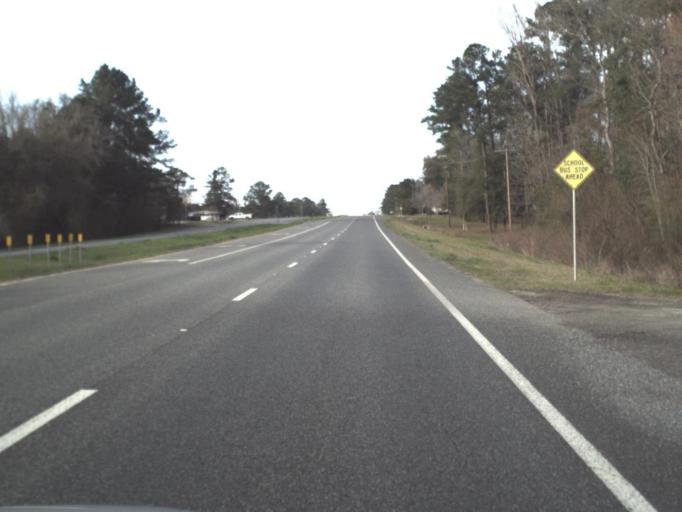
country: US
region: Florida
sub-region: Jefferson County
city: Monticello
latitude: 30.5788
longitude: -83.8699
